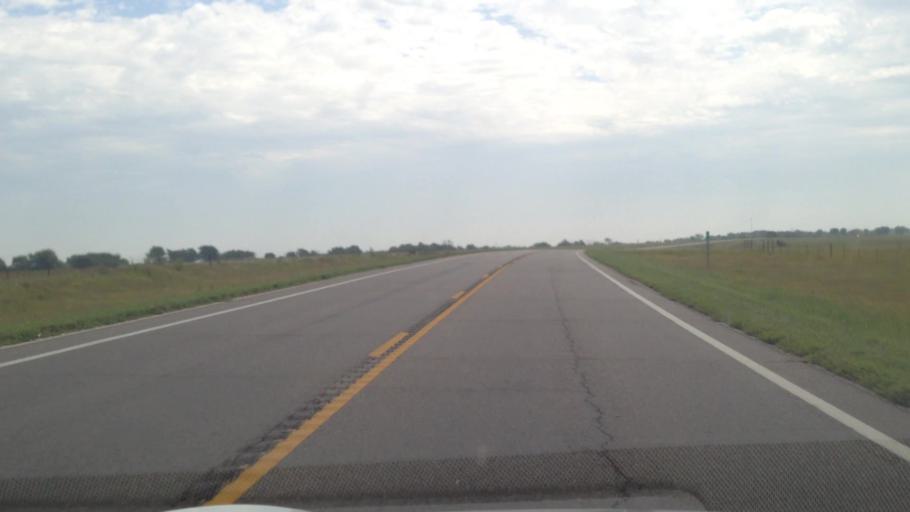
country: US
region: Kansas
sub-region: Bourbon County
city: Fort Scott
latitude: 37.8826
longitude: -95.0129
